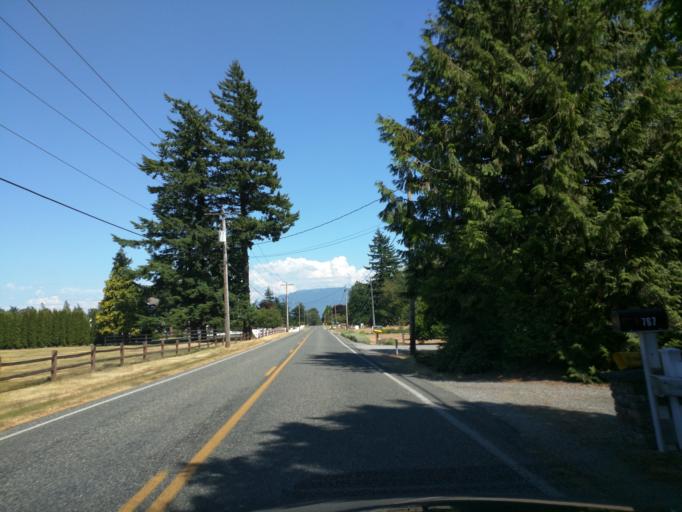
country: US
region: Washington
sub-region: Whatcom County
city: Lynden
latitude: 48.9100
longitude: -122.4485
